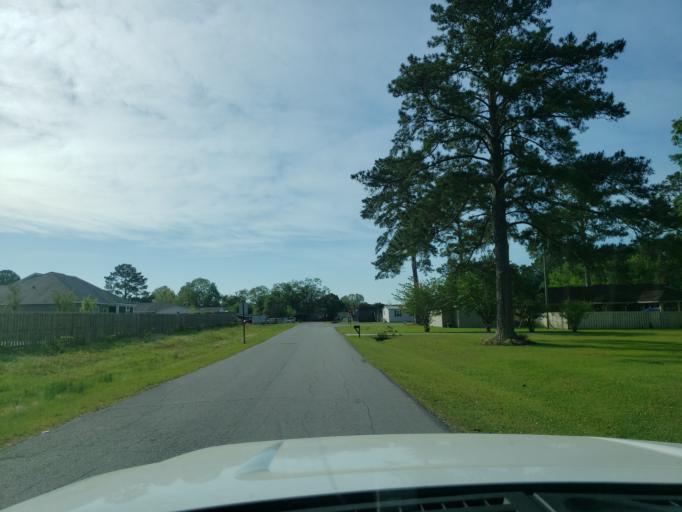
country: US
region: Georgia
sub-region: Chatham County
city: Georgetown
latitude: 32.0087
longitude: -81.2308
